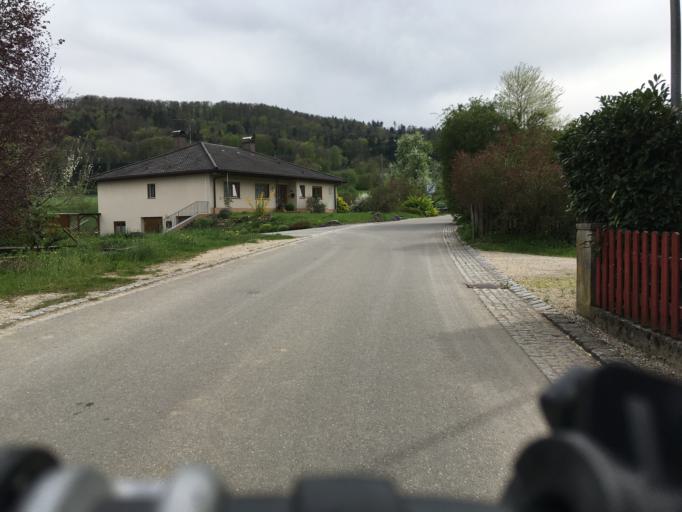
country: DE
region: Baden-Wuerttemberg
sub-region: Freiburg Region
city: Gailingen
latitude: 47.7138
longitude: 8.7671
